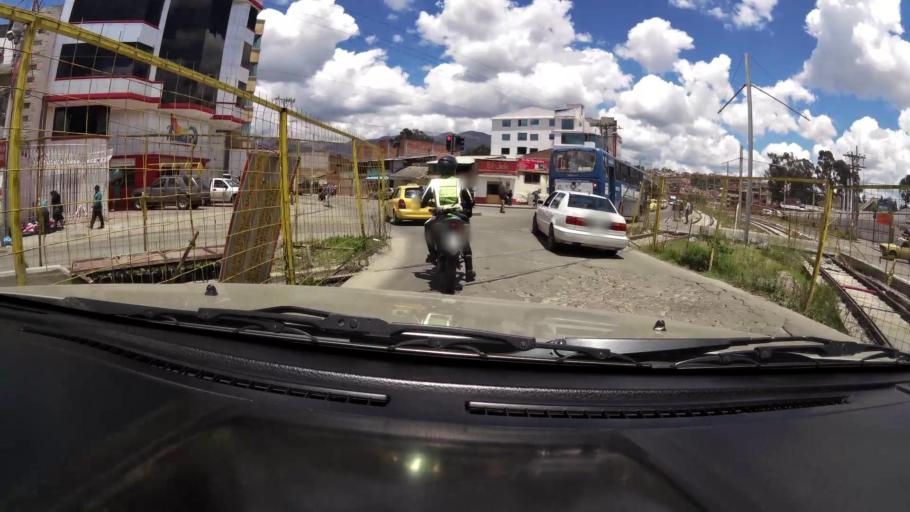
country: EC
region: Azuay
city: Cuenca
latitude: -2.8958
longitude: -79.0250
